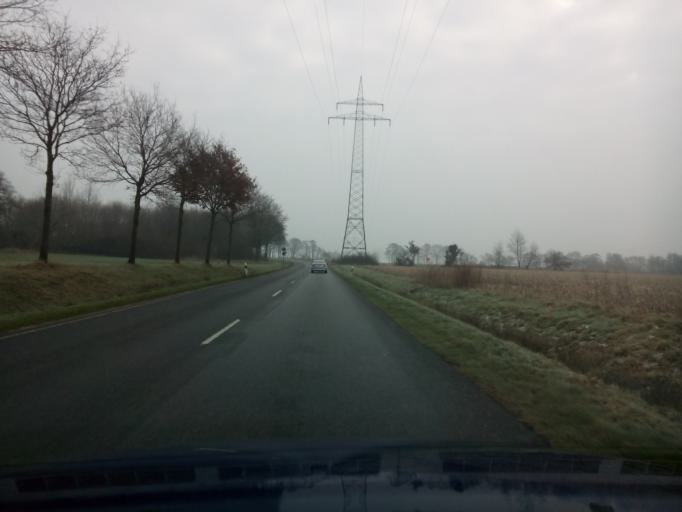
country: DE
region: Lower Saxony
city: Kuhrstedt
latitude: 53.6103
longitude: 8.8327
